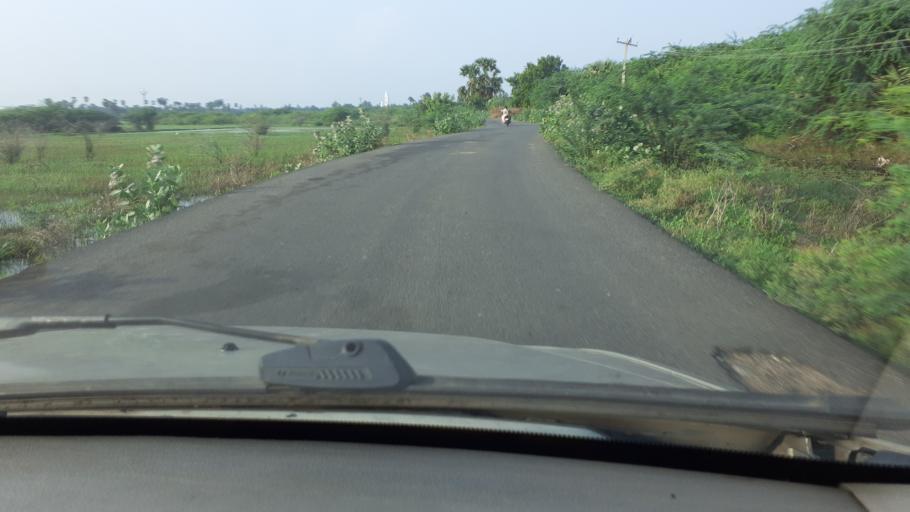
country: IN
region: Tamil Nadu
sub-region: Thoothukkudi
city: Alwar Tirunagari
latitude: 8.5830
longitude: 77.9789
